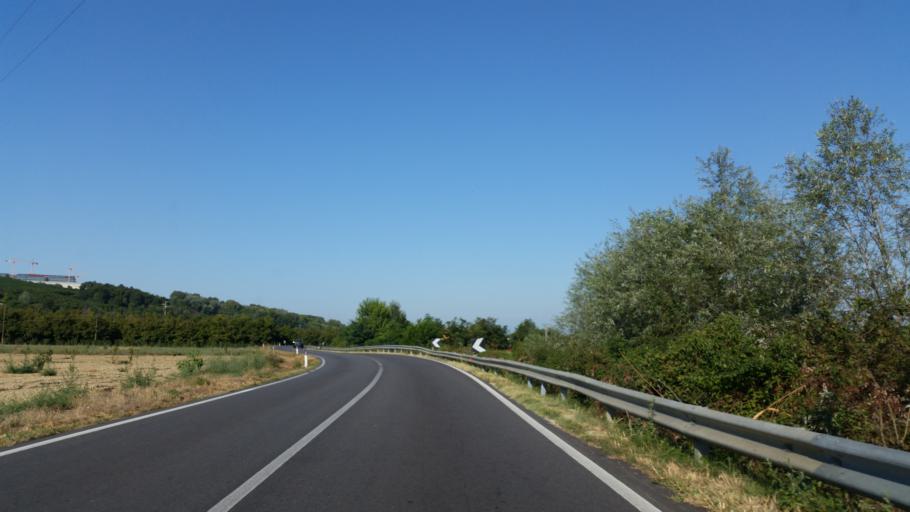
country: IT
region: Piedmont
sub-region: Provincia di Cuneo
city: Santa Vittoria d'Alba
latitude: 44.6838
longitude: 7.9508
